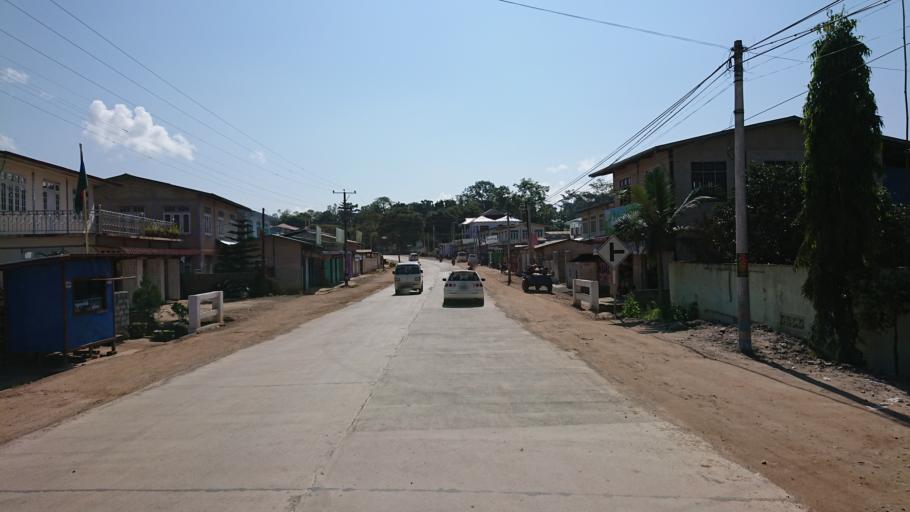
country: MM
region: Shan
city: Taunggyi
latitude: 20.8017
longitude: 97.1789
